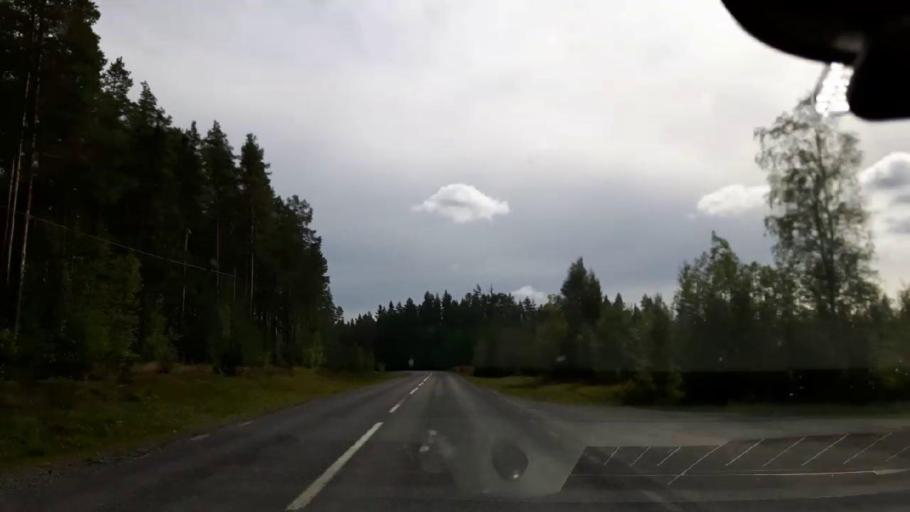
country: SE
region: Jaemtland
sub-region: Ragunda Kommun
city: Hammarstrand
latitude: 63.1406
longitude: 15.8621
